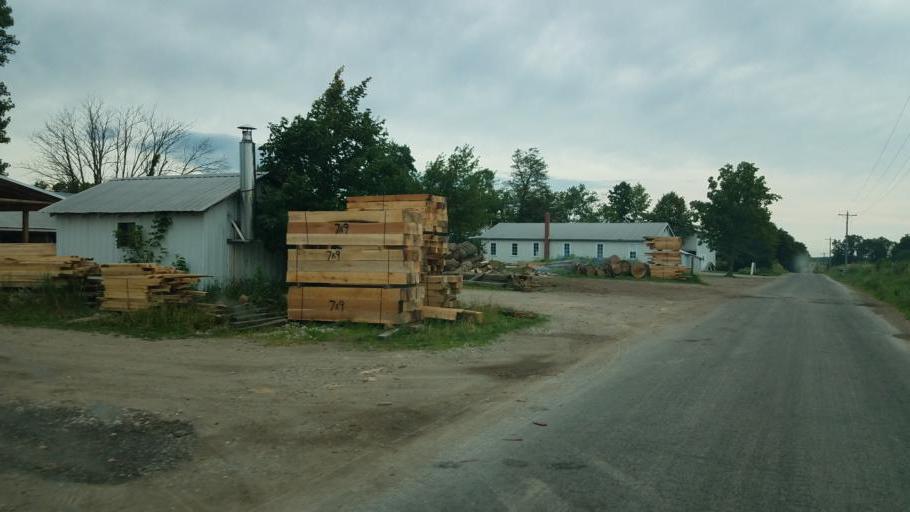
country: US
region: Ohio
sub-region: Ashland County
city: Ashland
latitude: 40.9342
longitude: -82.4072
